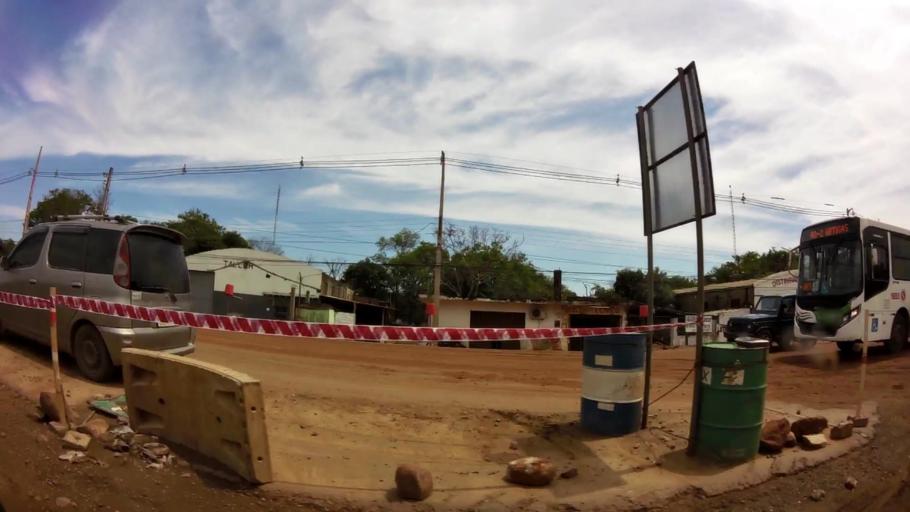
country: PY
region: Central
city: Colonia Mariano Roque Alonso
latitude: -25.2004
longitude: -57.5209
